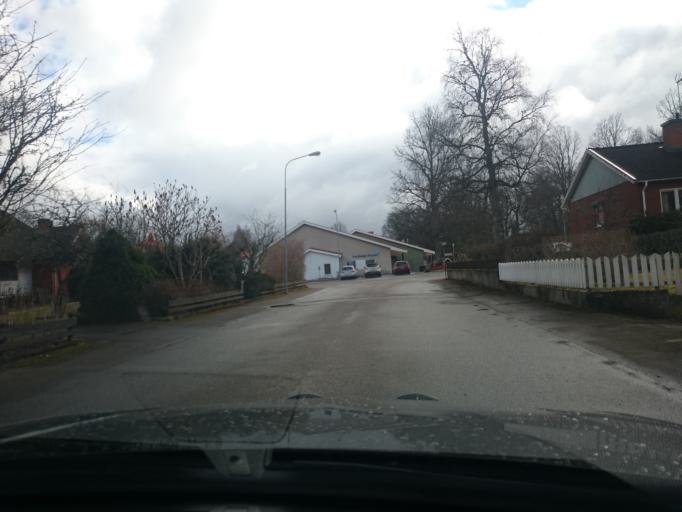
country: SE
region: Joenkoeping
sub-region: Vetlanda Kommun
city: Vetlanda
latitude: 57.3065
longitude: 15.1264
